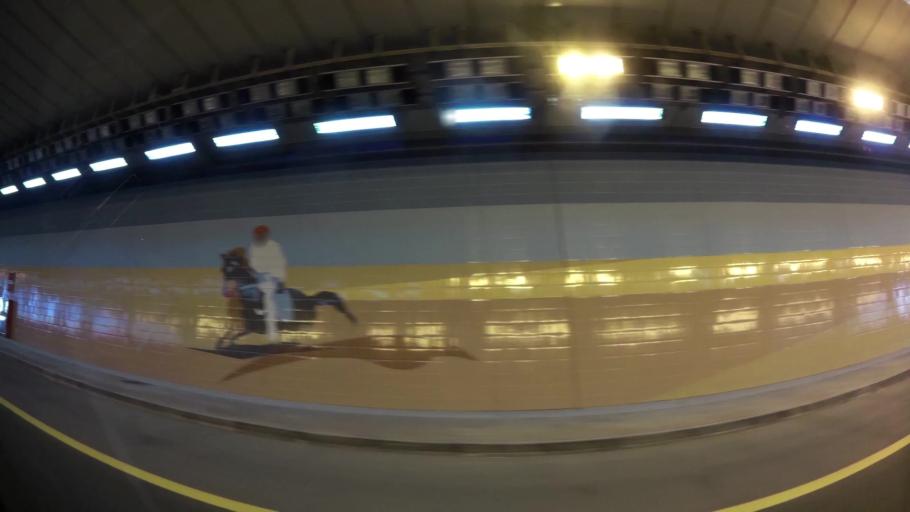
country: AE
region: Dubai
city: Dubai
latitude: 25.0533
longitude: 55.2490
